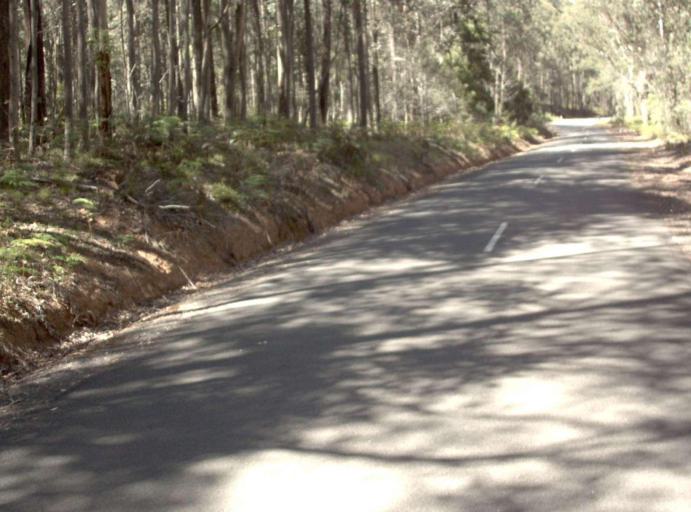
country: AU
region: New South Wales
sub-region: Bombala
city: Bombala
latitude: -37.0819
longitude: 148.7757
